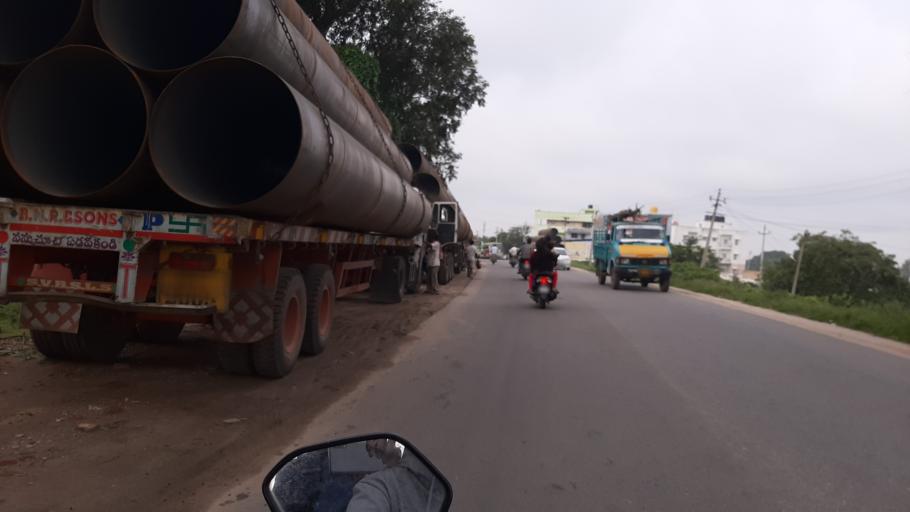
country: IN
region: Karnataka
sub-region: Bangalore Rural
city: Nelamangala
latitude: 12.9698
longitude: 77.4087
